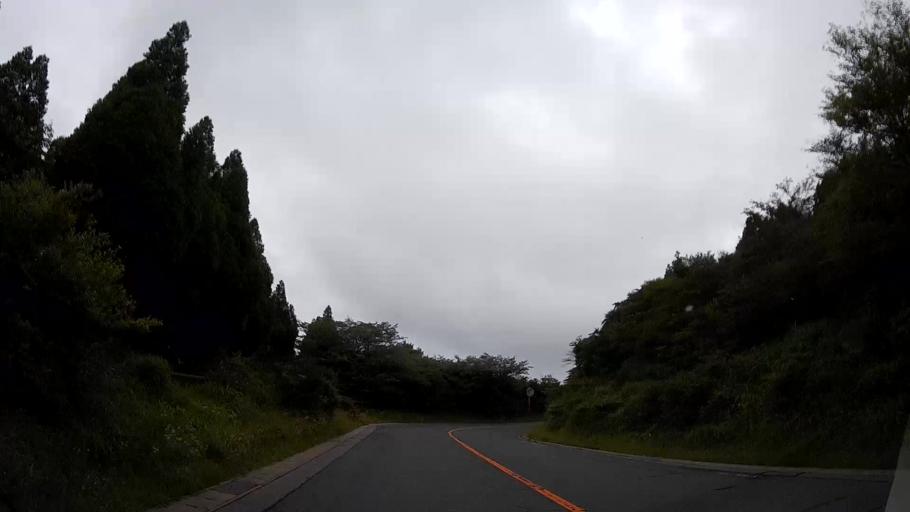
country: JP
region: Kumamoto
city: Aso
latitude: 32.8874
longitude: 131.0555
